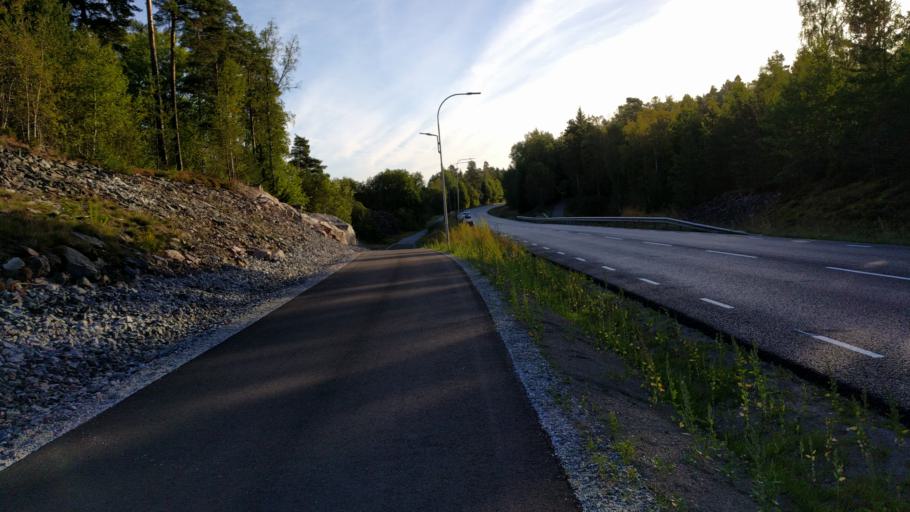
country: SE
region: Stockholm
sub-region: Taby Kommun
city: Taby
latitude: 59.4697
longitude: 18.0816
